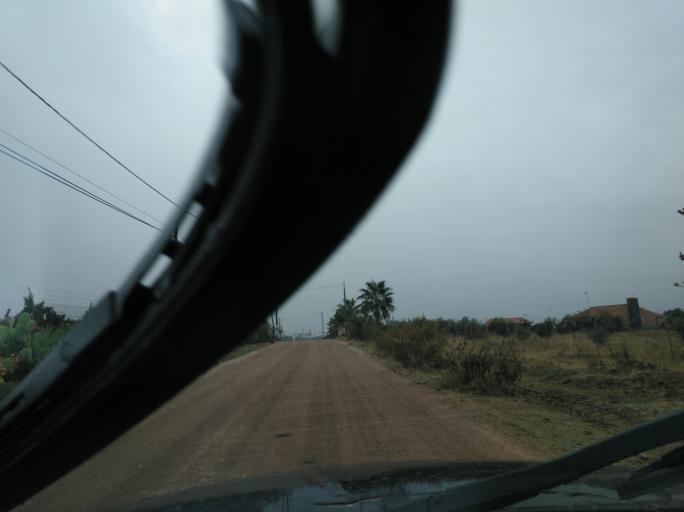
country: PT
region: Portalegre
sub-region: Campo Maior
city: Campo Maior
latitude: 38.9558
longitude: -7.0714
